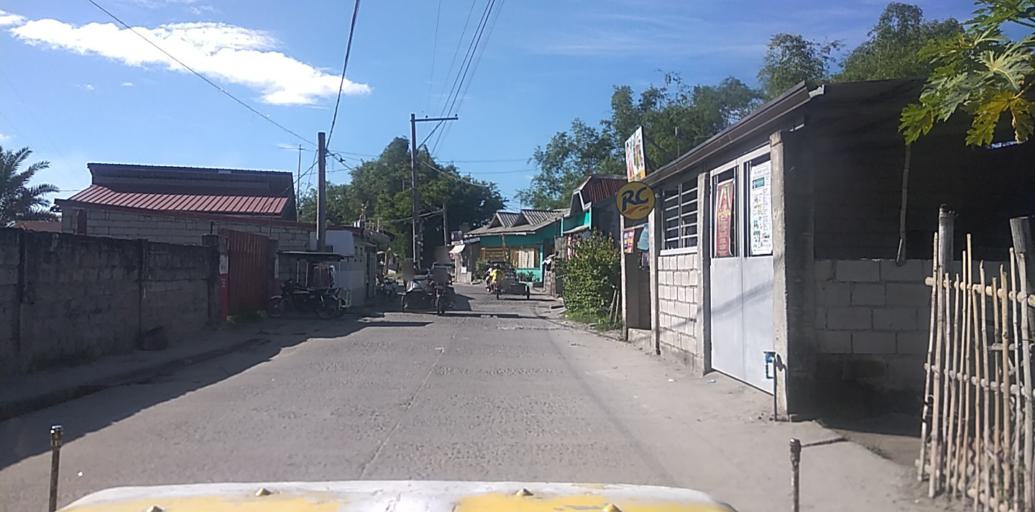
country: PH
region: Central Luzon
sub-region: Province of Pampanga
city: San Patricio
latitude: 15.0927
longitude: 120.7131
